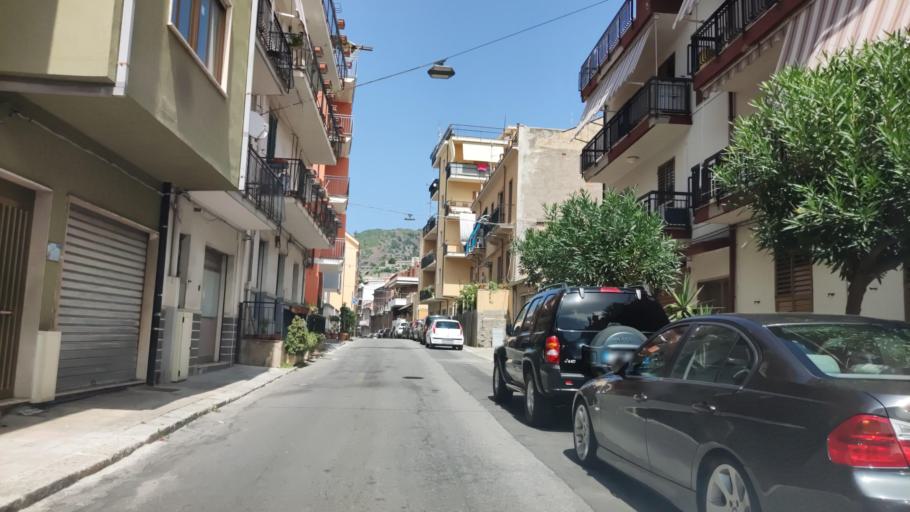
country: IT
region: Calabria
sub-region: Provincia di Reggio Calabria
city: Bagnara Calabra
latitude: 38.2845
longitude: 15.8007
